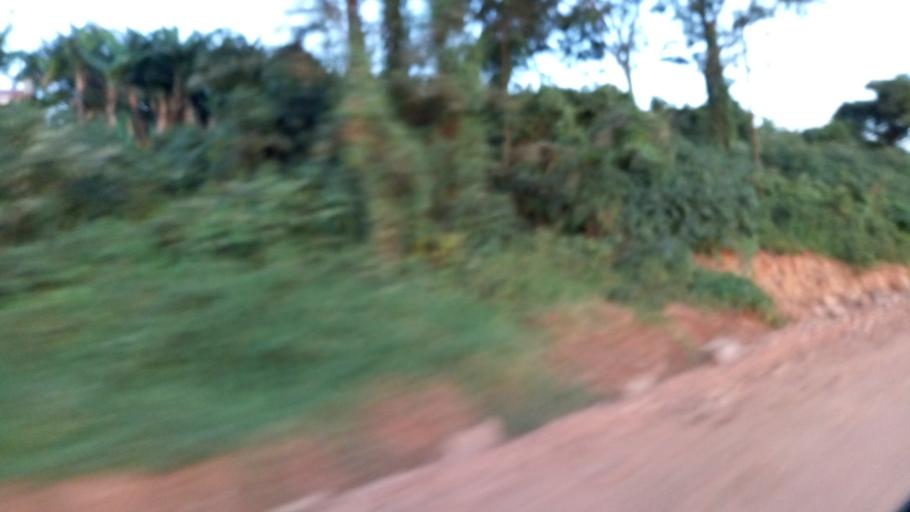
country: KE
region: Nyamira District
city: Nyamira
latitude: -0.5875
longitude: 35.0528
